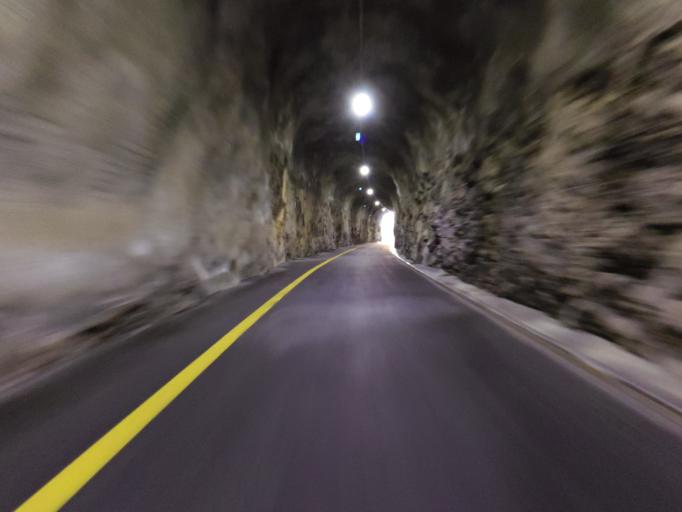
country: CH
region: Uri
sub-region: Uri
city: Bauen
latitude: 46.9442
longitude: 8.6200
